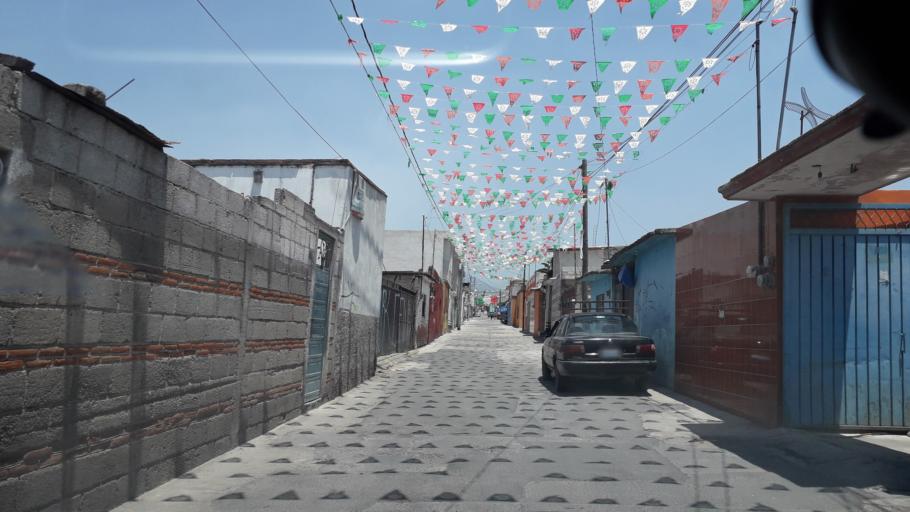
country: MX
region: Puebla
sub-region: Puebla
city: Santa Maria Xonacatepec
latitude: 19.0853
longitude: -98.1069
